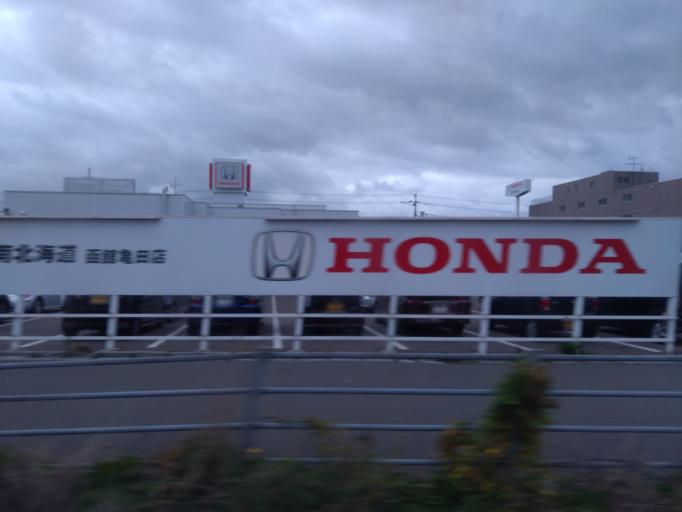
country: JP
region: Hokkaido
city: Hakodate
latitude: 41.7945
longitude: 140.7320
